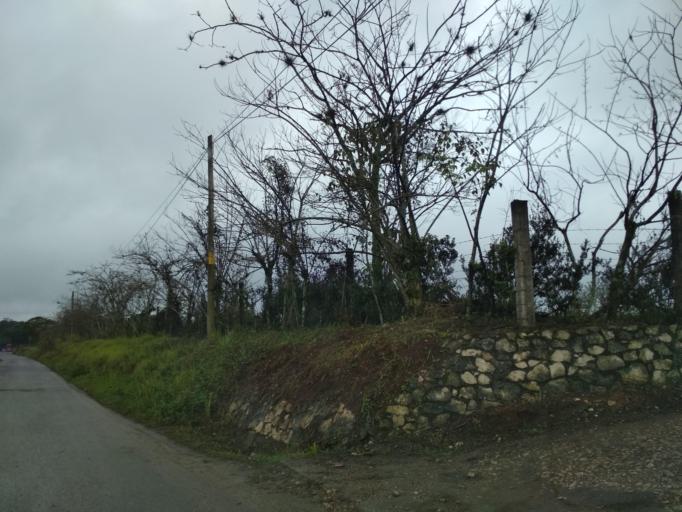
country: MX
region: Veracruz
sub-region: Amatlan de los Reyes
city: Centro de Readaptacion Social
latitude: 18.8371
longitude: -96.9390
